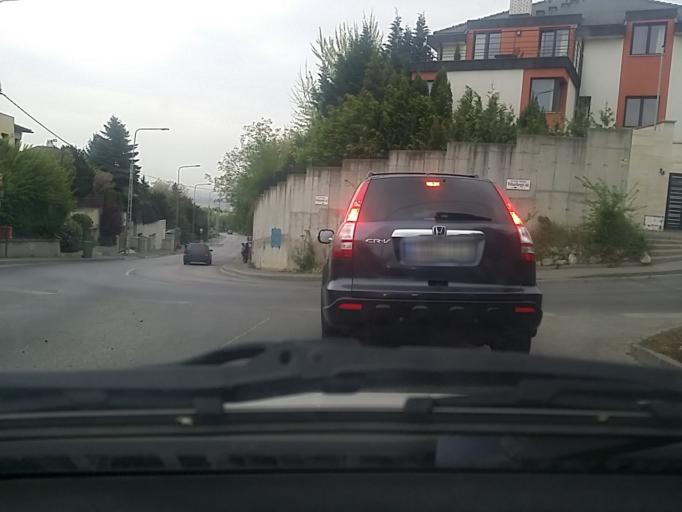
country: HU
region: Budapest
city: Budapest III. keruelet
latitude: 47.5542
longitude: 19.0206
